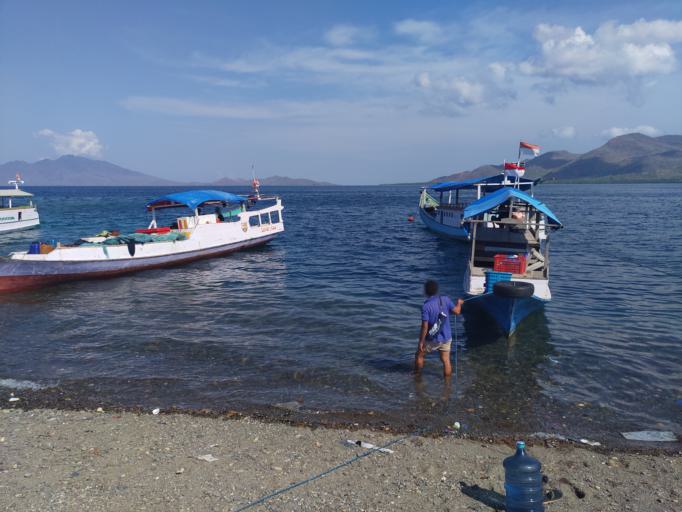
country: ID
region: East Nusa Tenggara
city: Nangahale
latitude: -8.5546
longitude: 122.5090
